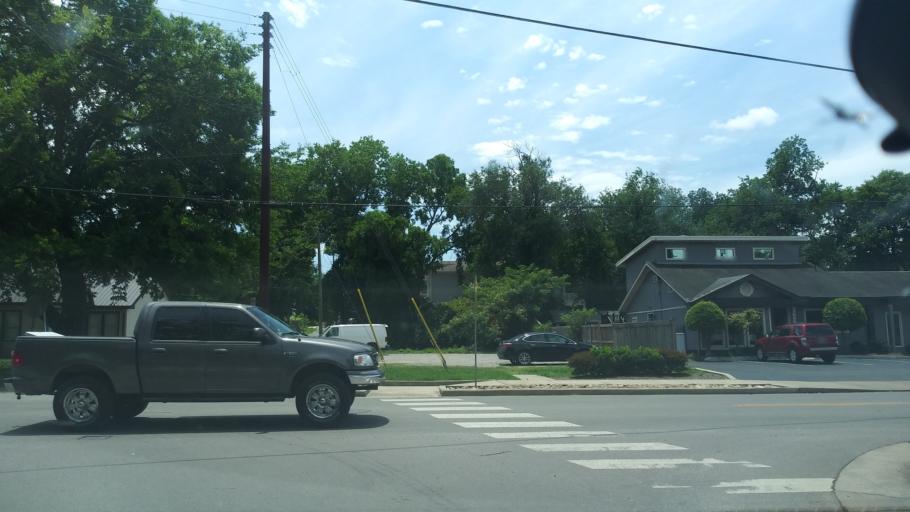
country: US
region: Tennessee
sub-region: Davidson County
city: Belle Meade
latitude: 36.1411
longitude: -86.8391
